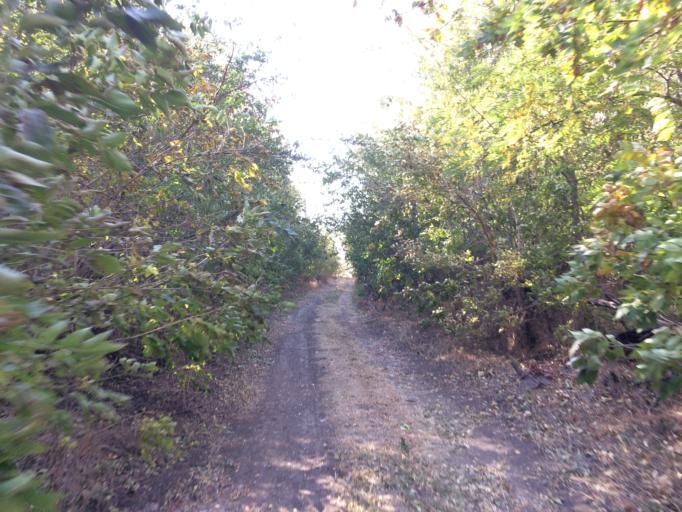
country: RU
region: Rostov
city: Tselina
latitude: 46.5218
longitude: 41.1816
